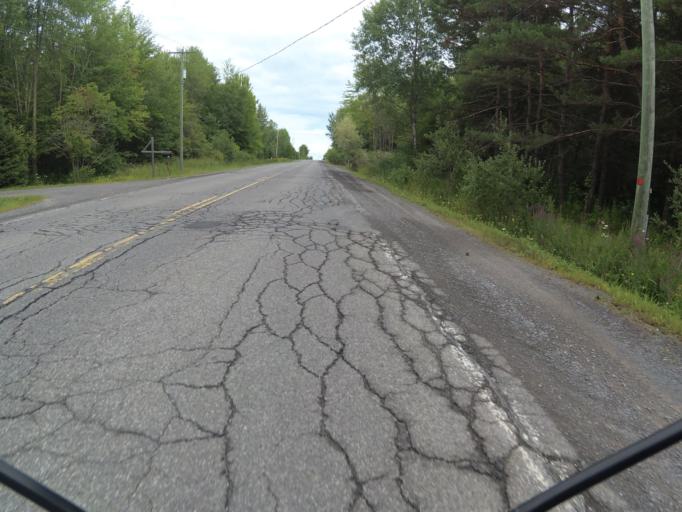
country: CA
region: Ontario
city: Bourget
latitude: 45.3740
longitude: -75.2693
